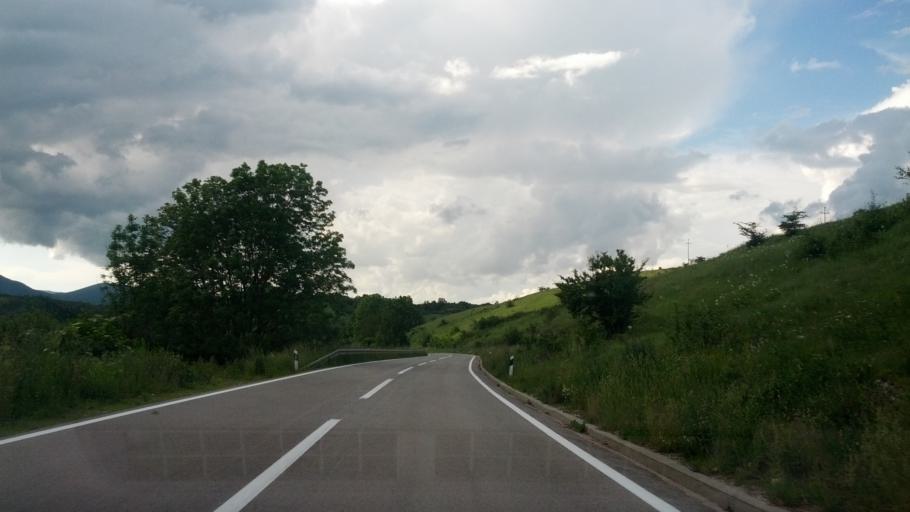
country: BA
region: Federation of Bosnia and Herzegovina
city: Izacic
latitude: 44.9146
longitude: 15.7184
